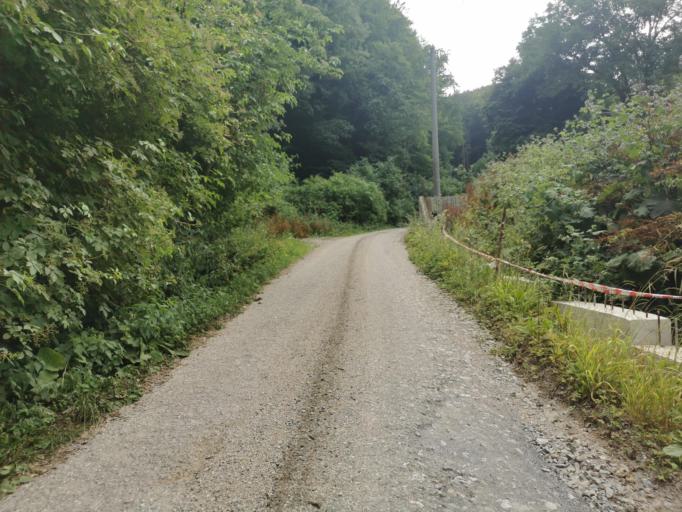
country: SK
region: Trenciansky
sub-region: Okres Myjava
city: Myjava
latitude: 48.7328
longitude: 17.5122
